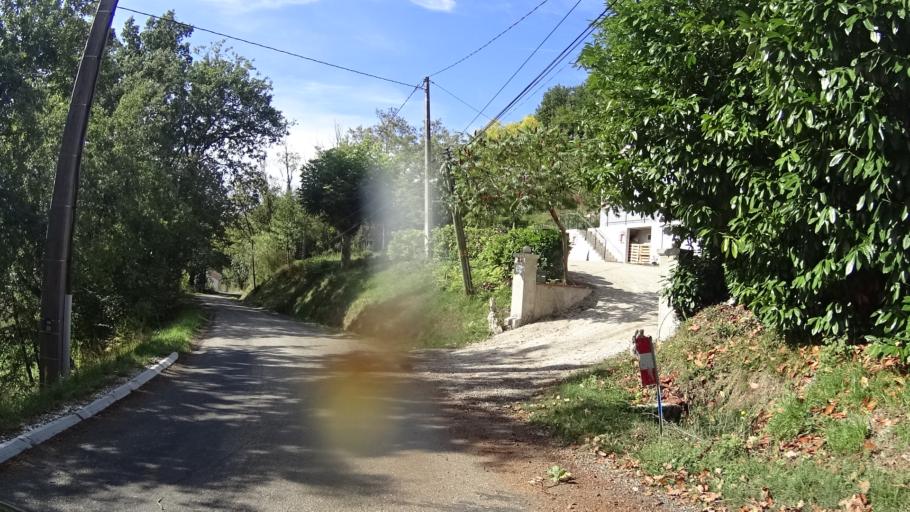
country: FR
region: Aquitaine
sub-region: Departement du Lot-et-Garonne
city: Laroque-Timbaut
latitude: 44.2174
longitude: 0.7468
